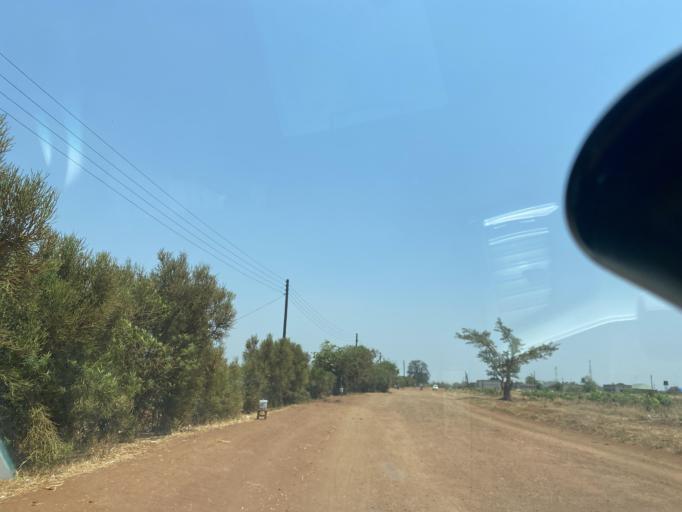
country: ZM
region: Southern
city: Nakambala
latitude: -15.5161
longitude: 27.9347
